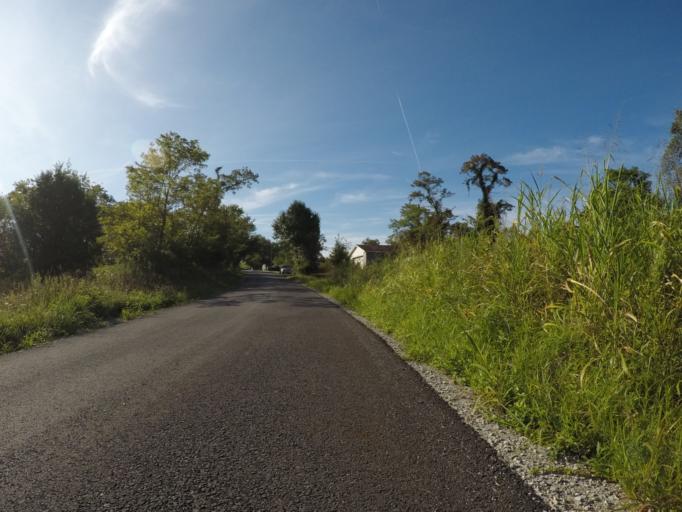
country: US
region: Ohio
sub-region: Lawrence County
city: Burlington
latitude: 38.5257
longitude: -82.5255
